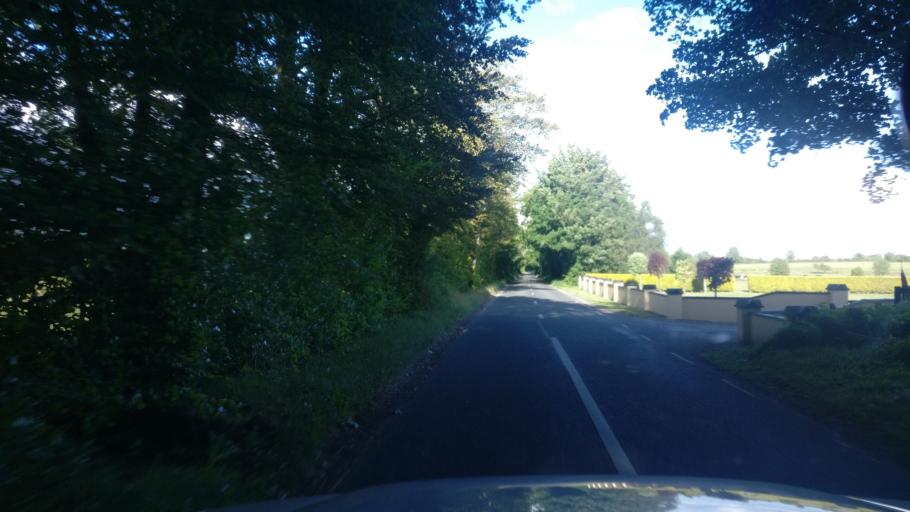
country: IE
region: Connaught
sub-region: County Galway
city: Ballinasloe
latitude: 53.2243
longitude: -8.2096
